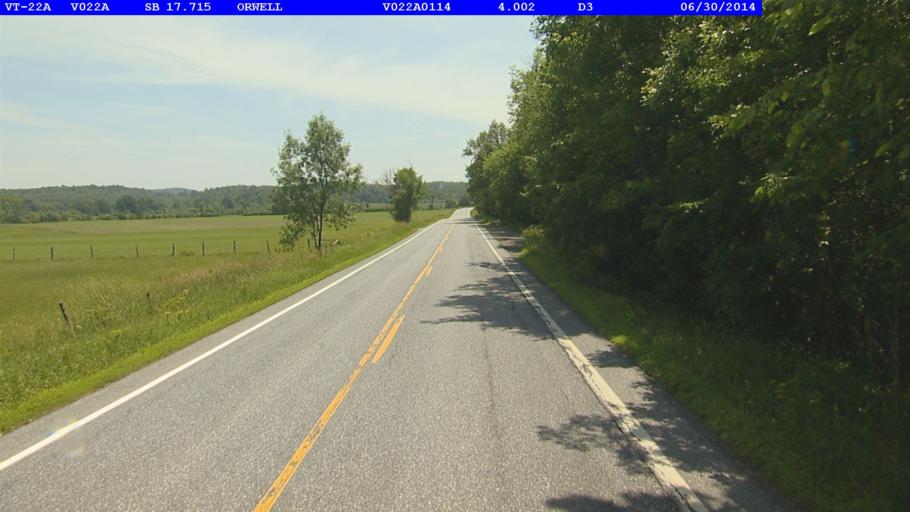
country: US
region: New York
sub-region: Essex County
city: Ticonderoga
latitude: 43.8146
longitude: -73.3053
